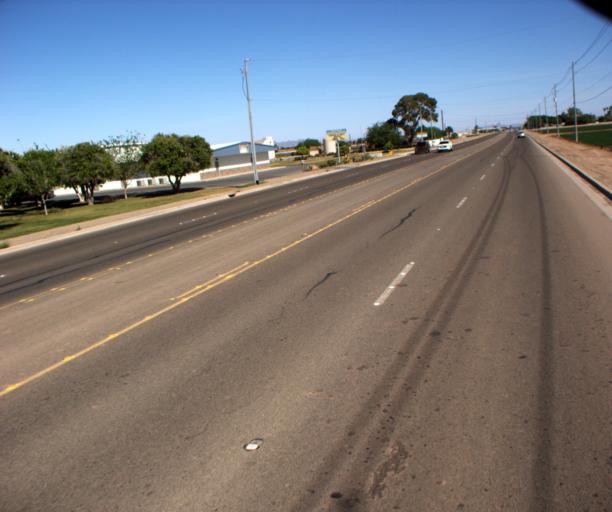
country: US
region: Arizona
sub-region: Yuma County
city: Yuma
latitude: 32.6566
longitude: -114.6500
